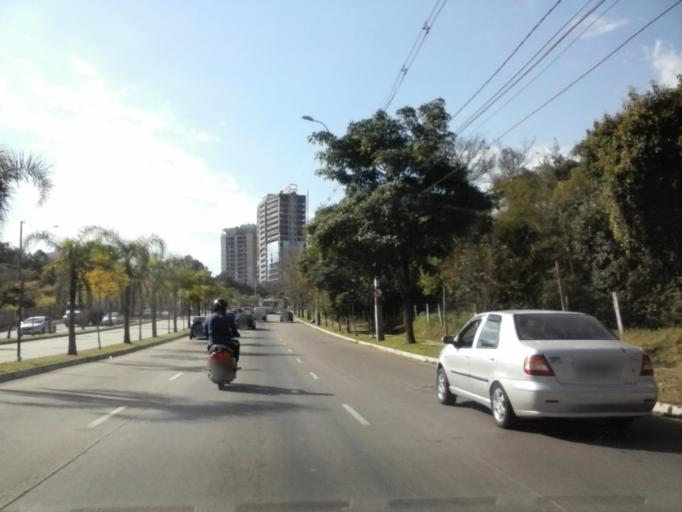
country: BR
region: Rio Grande do Sul
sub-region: Porto Alegre
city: Porto Alegre
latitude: -30.0464
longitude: -51.1776
